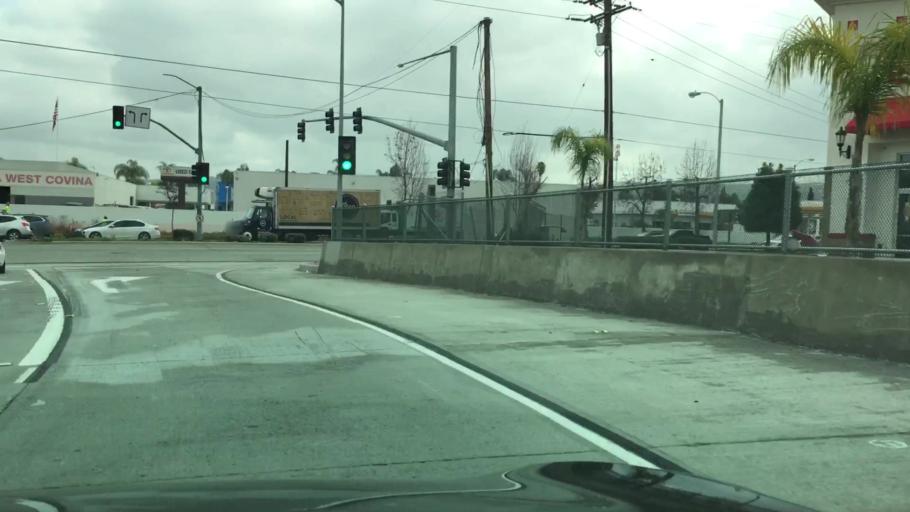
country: US
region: California
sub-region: Los Angeles County
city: Covina
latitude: 34.0712
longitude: -117.9082
